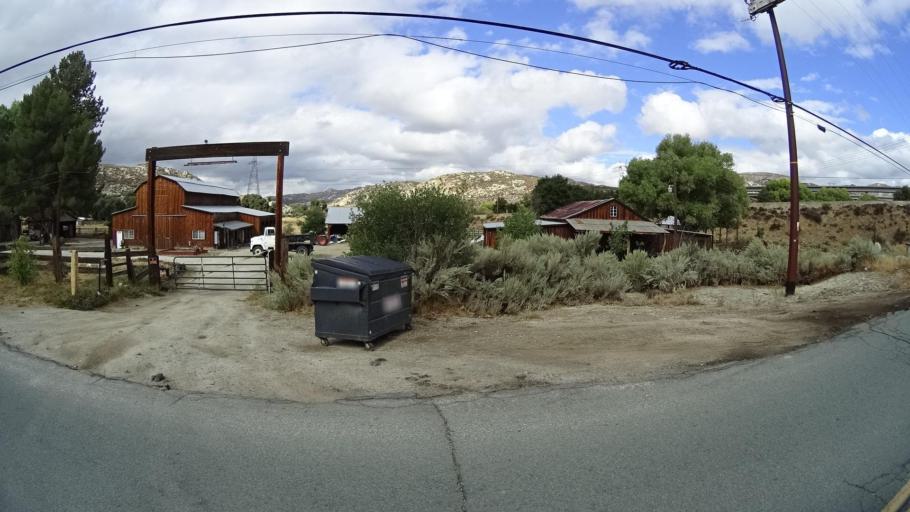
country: US
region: California
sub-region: San Diego County
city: Campo
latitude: 32.7235
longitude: -116.4271
